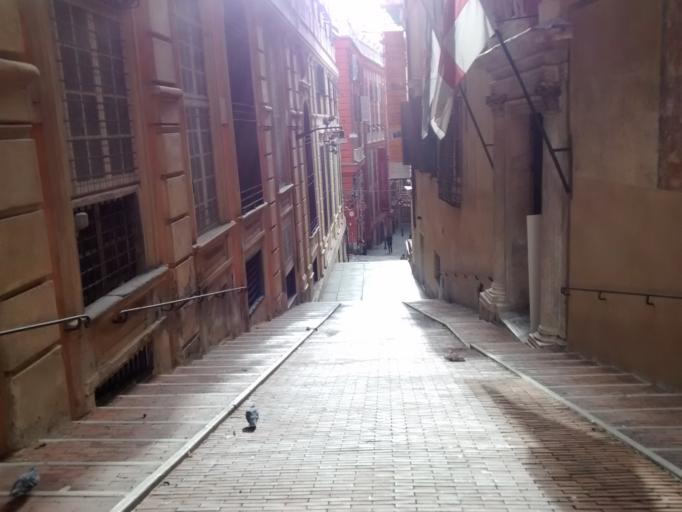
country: IT
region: Liguria
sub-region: Provincia di Genova
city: San Teodoro
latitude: 44.4119
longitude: 8.9318
